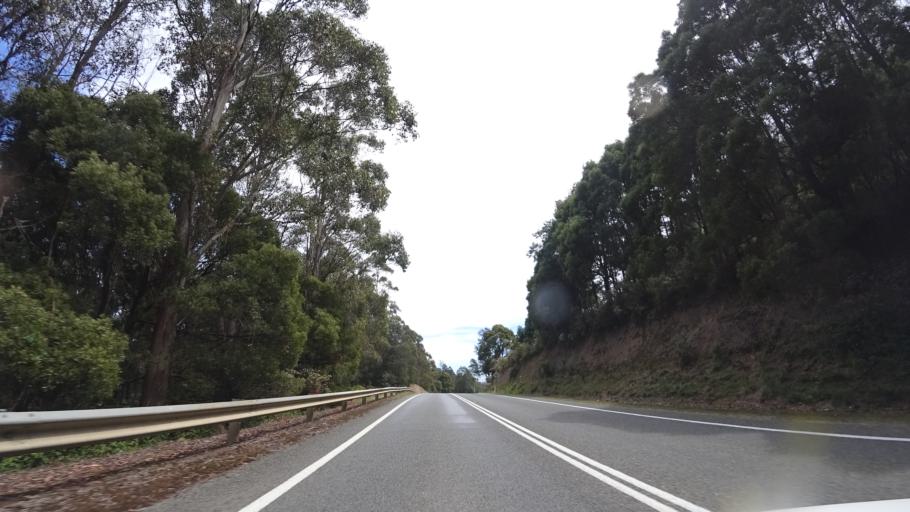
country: AU
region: Tasmania
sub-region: Dorset
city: Scottsdale
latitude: -41.2022
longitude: 147.6706
